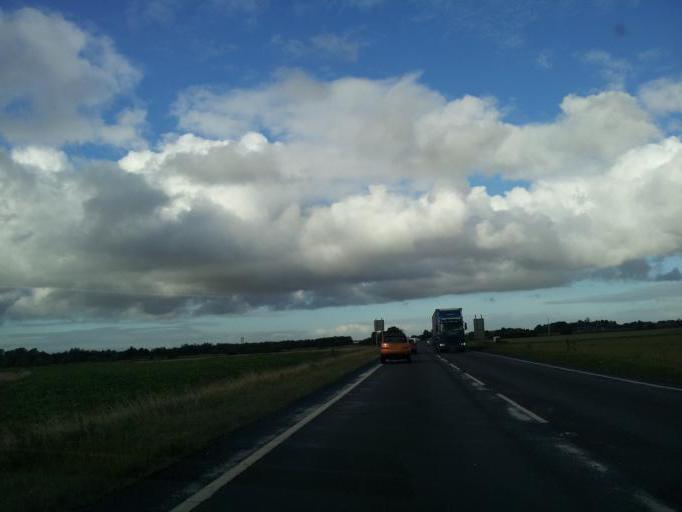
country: GB
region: England
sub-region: Norfolk
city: Terrington Saint John
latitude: 52.7498
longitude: 0.2458
